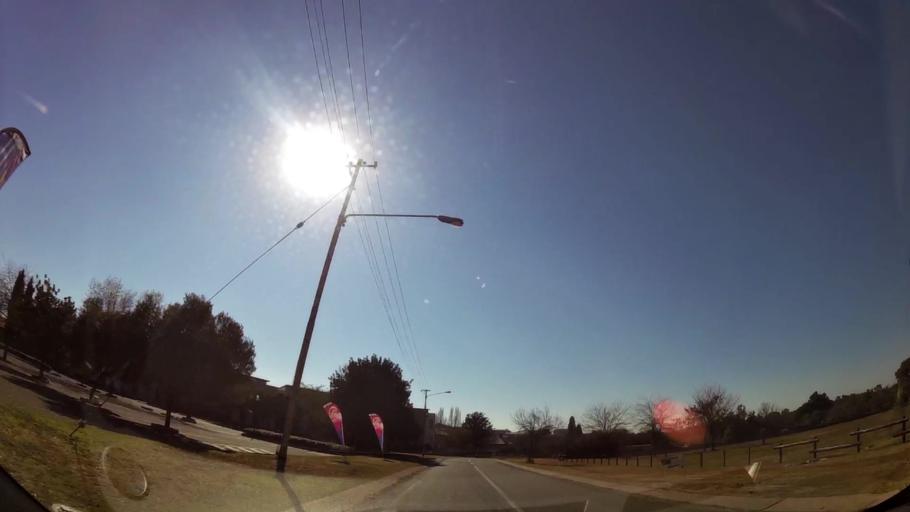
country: ZA
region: Gauteng
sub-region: City of Tshwane Metropolitan Municipality
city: Centurion
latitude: -25.8443
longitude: 28.2094
